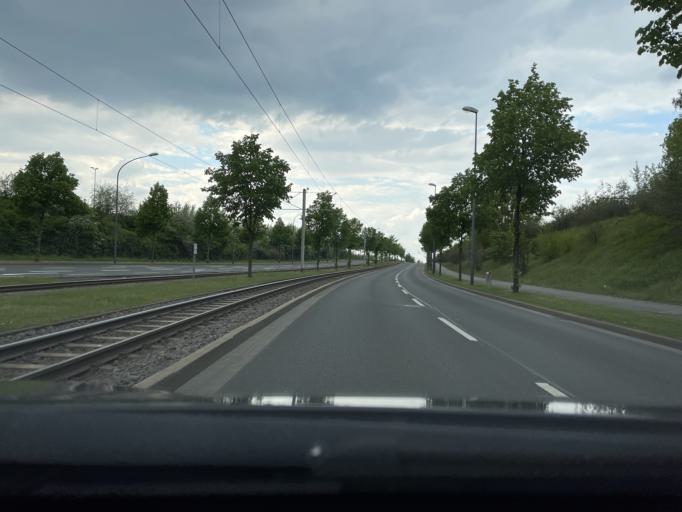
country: DE
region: North Rhine-Westphalia
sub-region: Regierungsbezirk Dusseldorf
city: Essen
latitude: 51.4549
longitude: 6.9906
